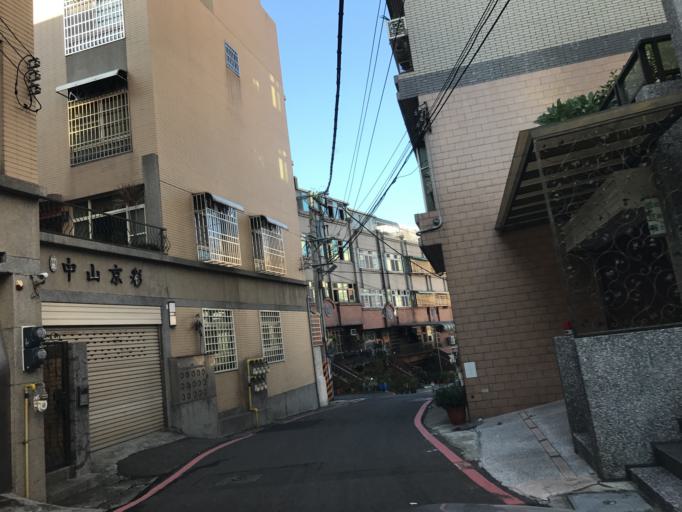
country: TW
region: Taiwan
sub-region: Hsinchu
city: Hsinchu
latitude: 24.7946
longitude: 120.9576
